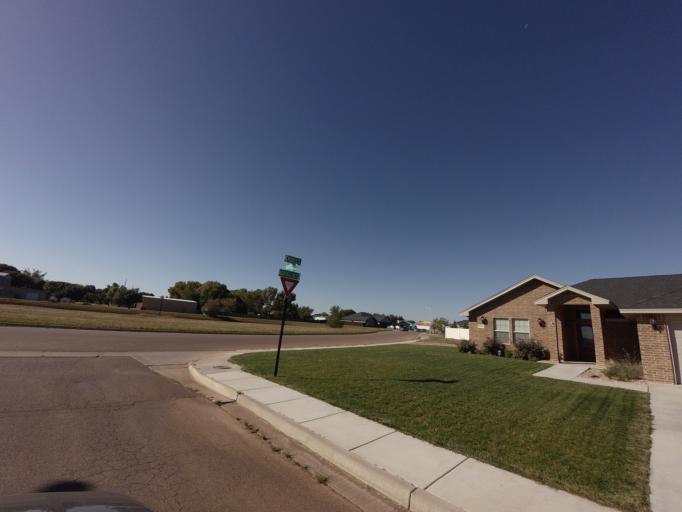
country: US
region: New Mexico
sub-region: Curry County
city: Clovis
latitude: 34.4296
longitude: -103.1691
